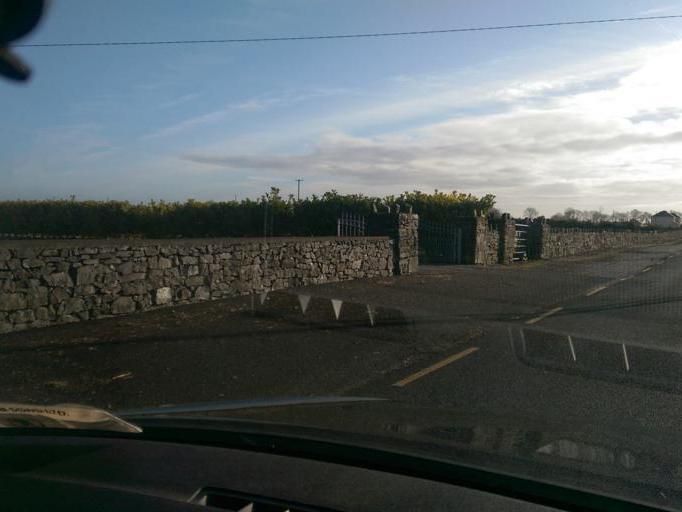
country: IE
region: Connaught
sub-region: County Galway
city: Athenry
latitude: 53.4213
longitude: -8.5665
